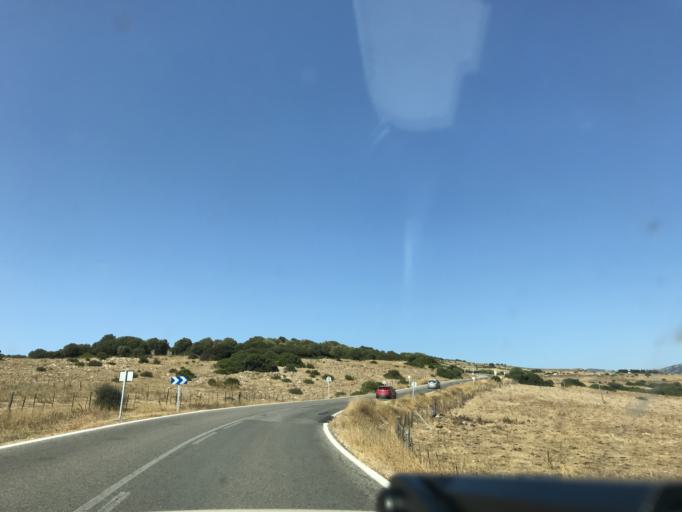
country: ES
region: Andalusia
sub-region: Provincia de Cadiz
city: Zahara de los Atunes
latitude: 36.1003
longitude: -5.7467
